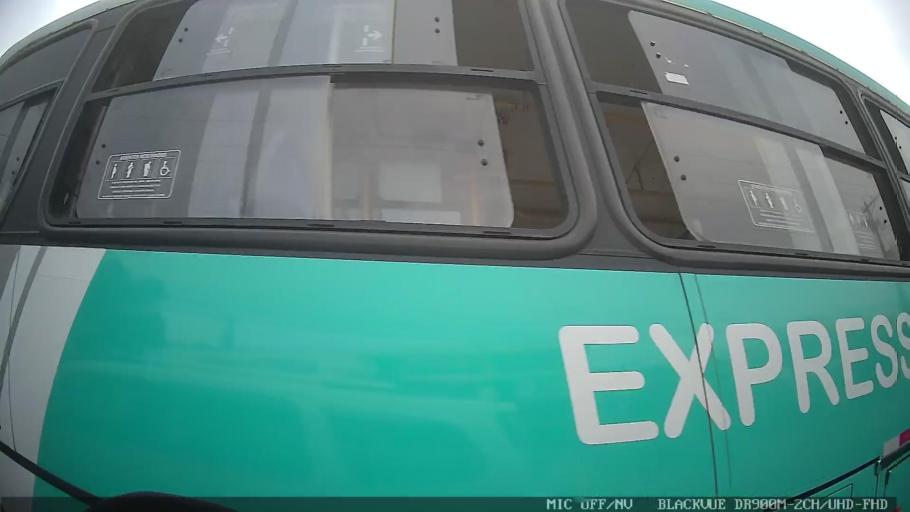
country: BR
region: Sao Paulo
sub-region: Itaquaquecetuba
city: Itaquaquecetuba
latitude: -23.5010
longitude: -46.3500
